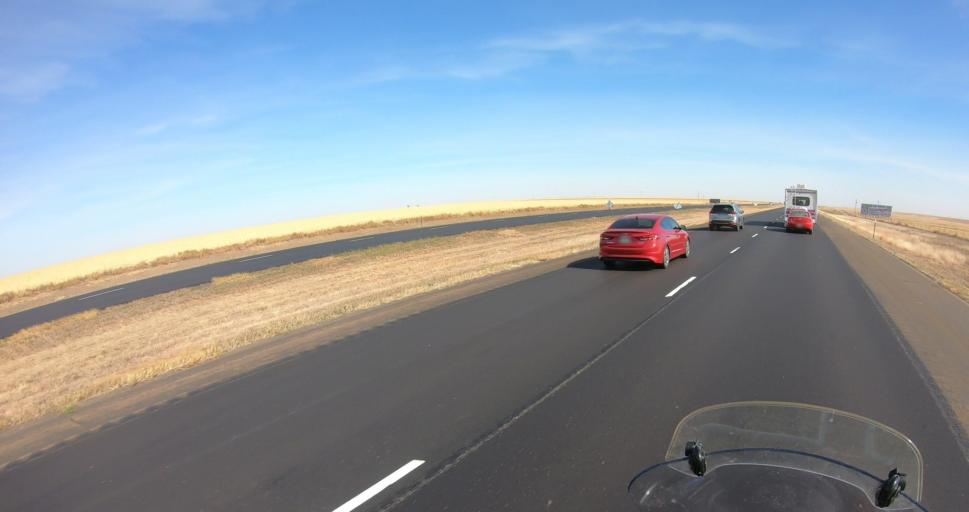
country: US
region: Kansas
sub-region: Thomas County
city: Colby
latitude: 39.3545
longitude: -101.3377
